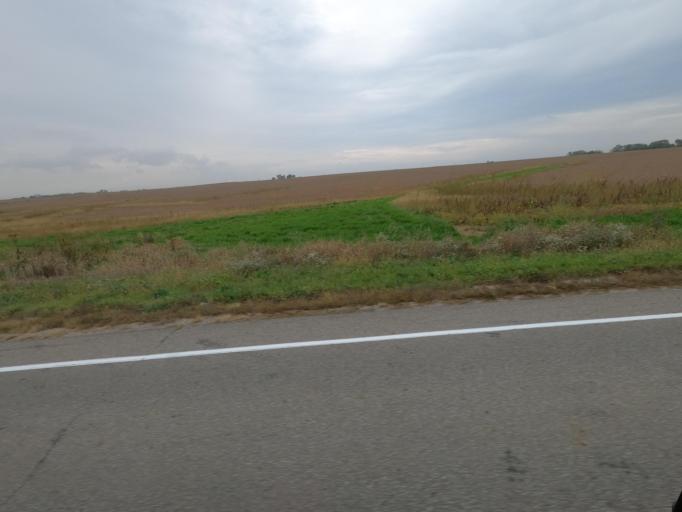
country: US
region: Iowa
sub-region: Van Buren County
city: Keosauqua
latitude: 40.8133
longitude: -91.8017
